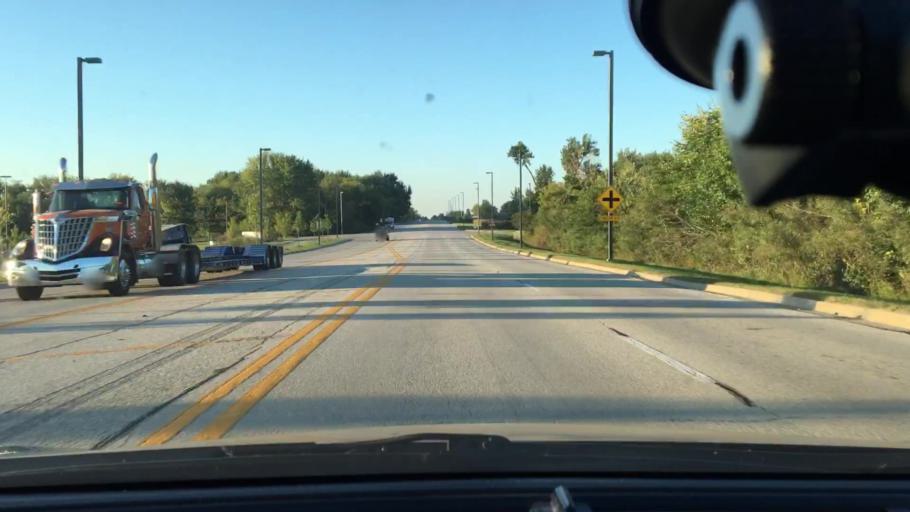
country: US
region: Illinois
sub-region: Kane County
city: East Dundee
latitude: 42.0723
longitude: -88.2236
